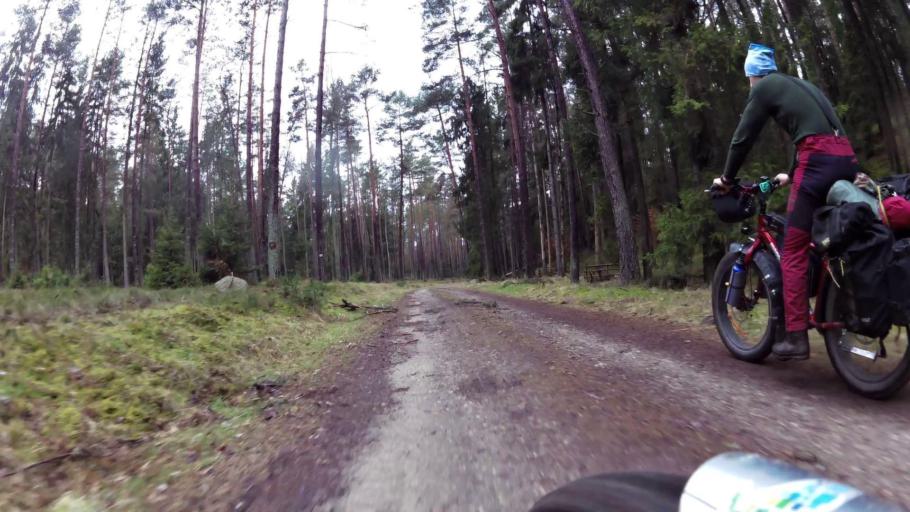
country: PL
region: Pomeranian Voivodeship
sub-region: Powiat bytowski
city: Borzytuchom
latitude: 54.2566
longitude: 17.3162
